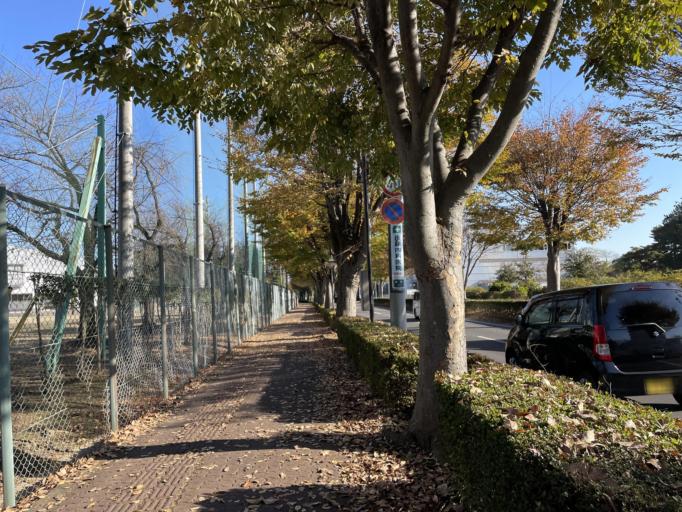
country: JP
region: Gunma
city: Tatebayashi
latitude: 36.2449
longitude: 139.5436
